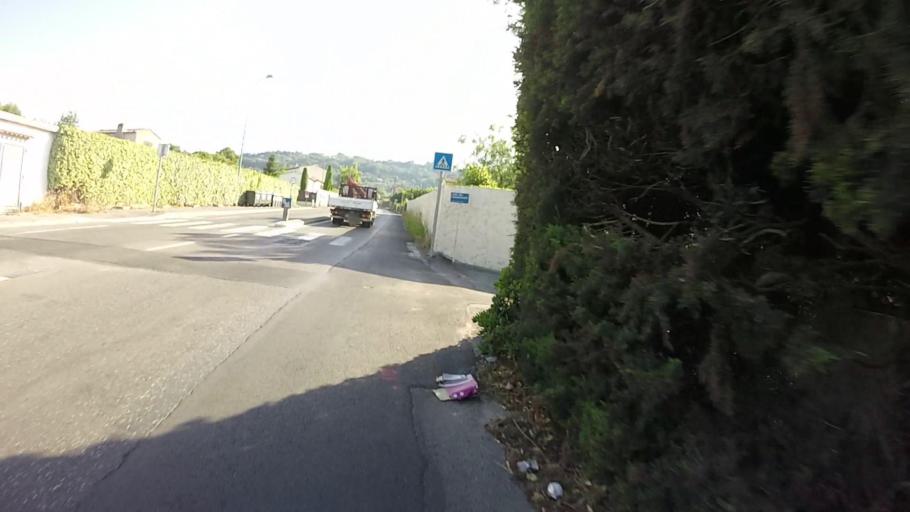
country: FR
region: Provence-Alpes-Cote d'Azur
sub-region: Departement des Alpes-Maritimes
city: Mouans-Sartoux
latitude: 43.6240
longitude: 6.9742
